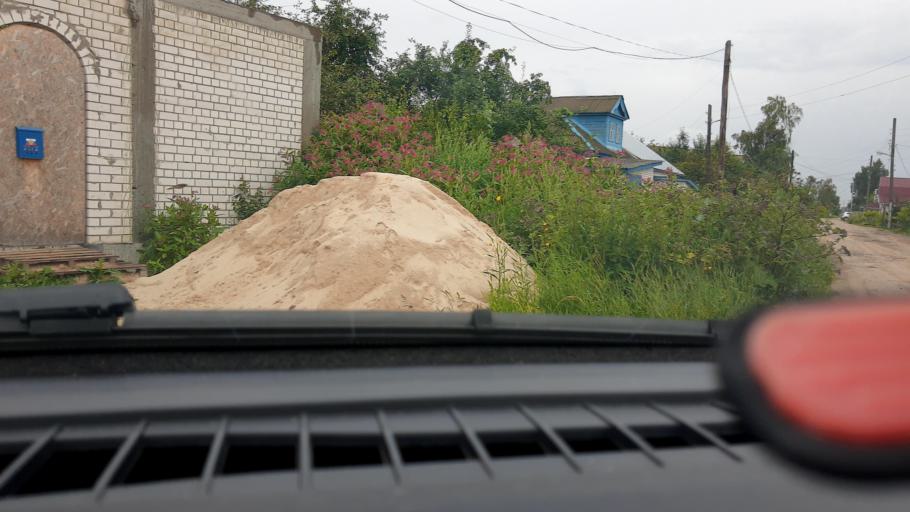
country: RU
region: Nizjnij Novgorod
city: Bor
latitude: 56.3528
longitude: 44.1301
